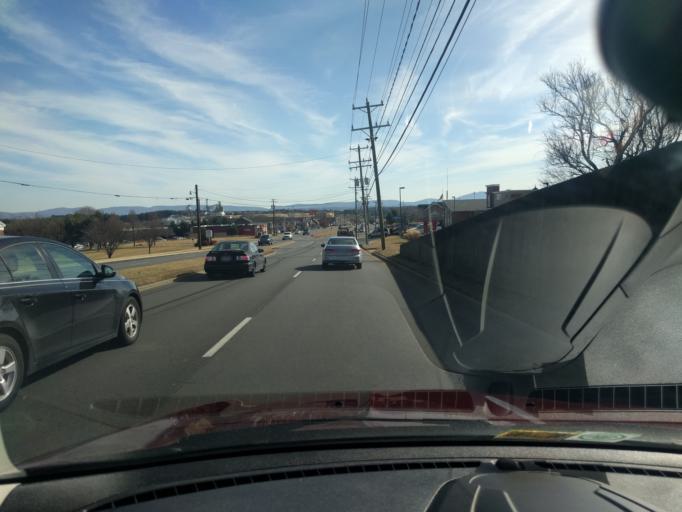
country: US
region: Virginia
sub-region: City of Staunton
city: Staunton
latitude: 38.1378
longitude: -79.0471
